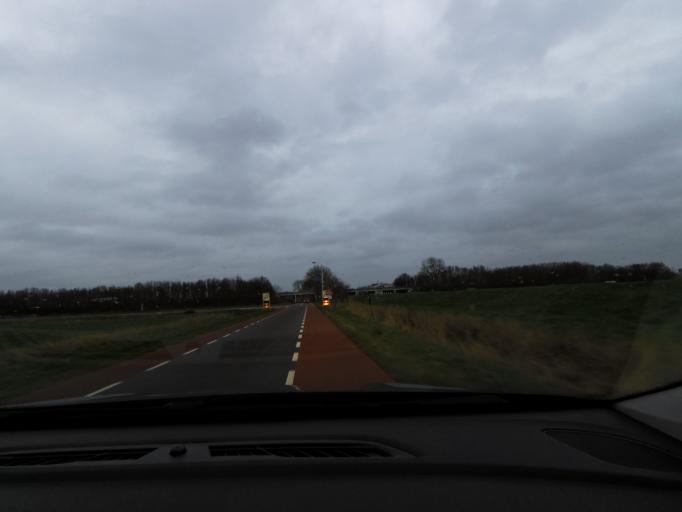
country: NL
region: North Brabant
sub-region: Gemeente Waalwijk
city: Waspik
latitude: 51.6972
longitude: 4.9842
